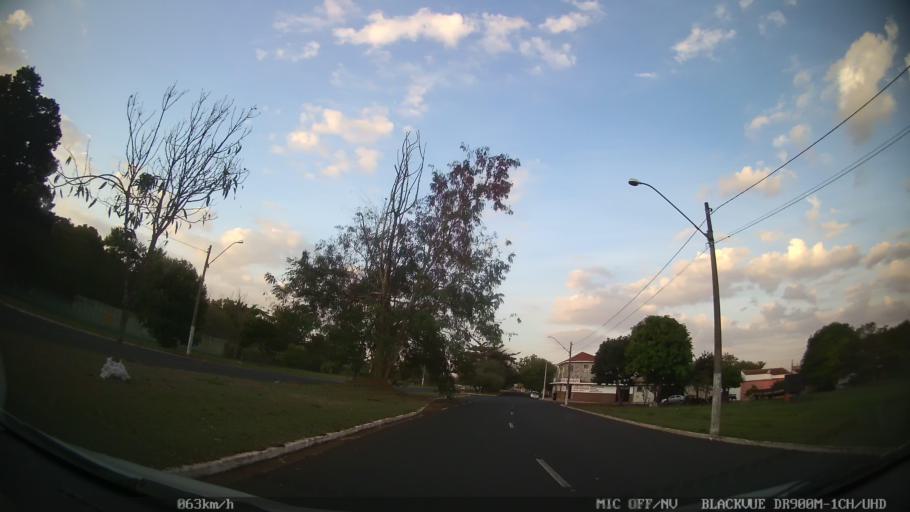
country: BR
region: Sao Paulo
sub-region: Ribeirao Preto
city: Ribeirao Preto
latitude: -21.1277
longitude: -47.8330
